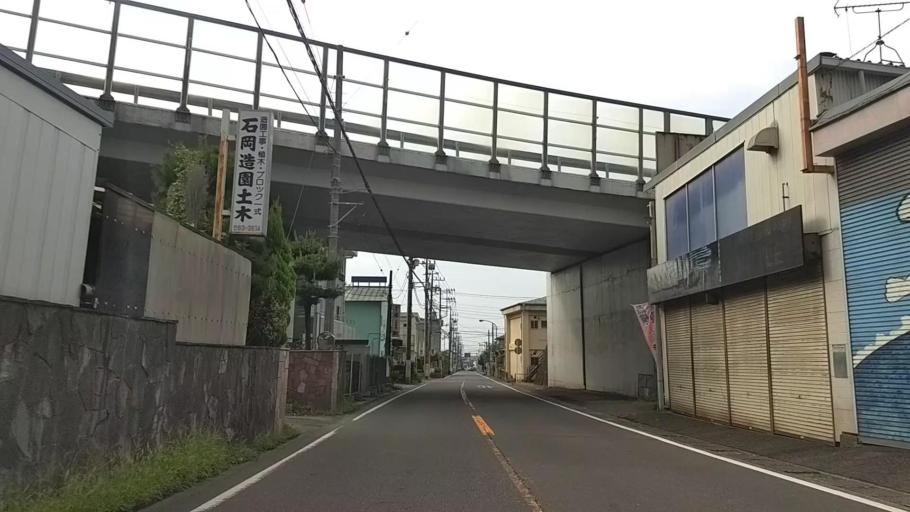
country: JP
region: Kanagawa
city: Hadano
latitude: 35.3412
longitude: 139.1519
